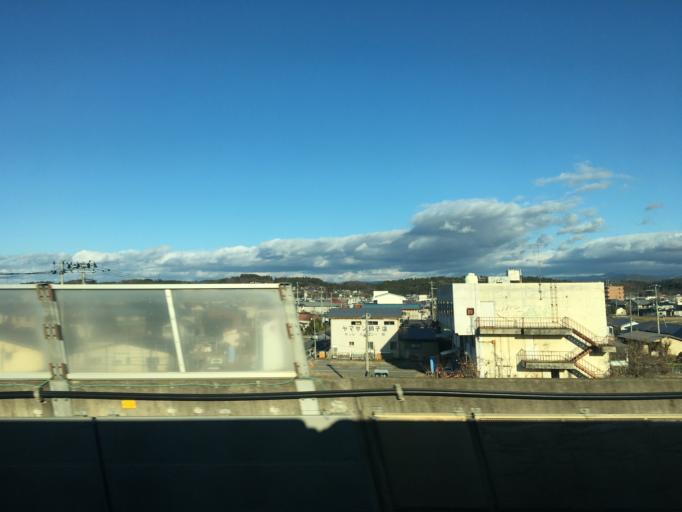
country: JP
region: Iwate
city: Mizusawa
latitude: 39.1848
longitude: 141.1667
